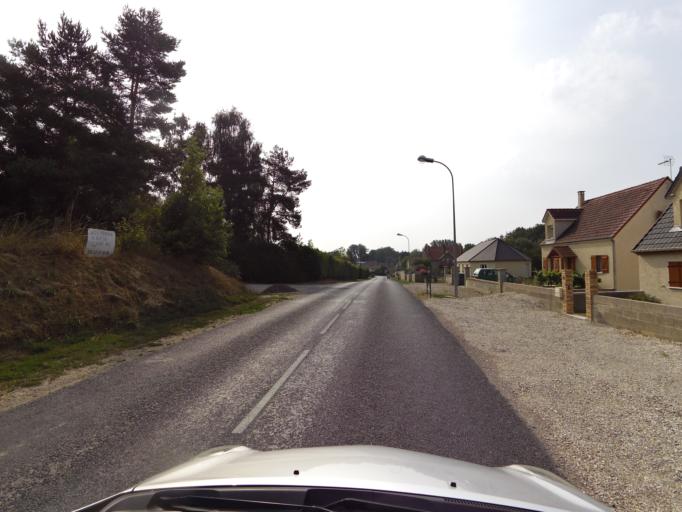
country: FR
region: Champagne-Ardenne
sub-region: Departement de la Marne
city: Fismes
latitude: 49.2745
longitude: 3.6975
